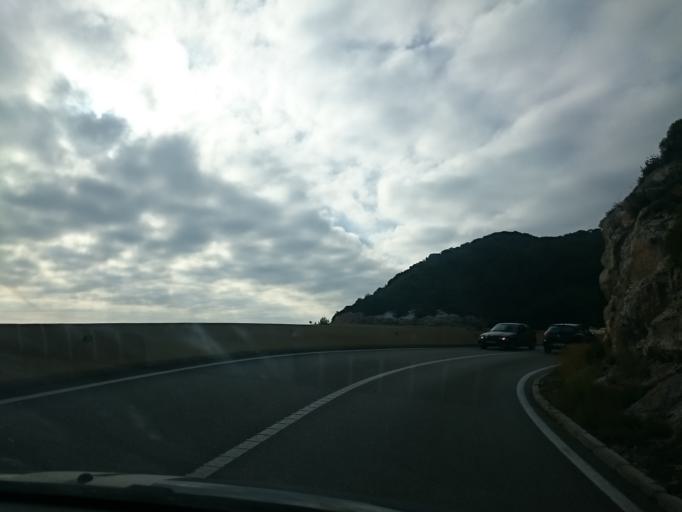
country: ES
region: Catalonia
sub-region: Provincia de Barcelona
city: Sitges
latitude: 41.2363
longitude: 1.8569
